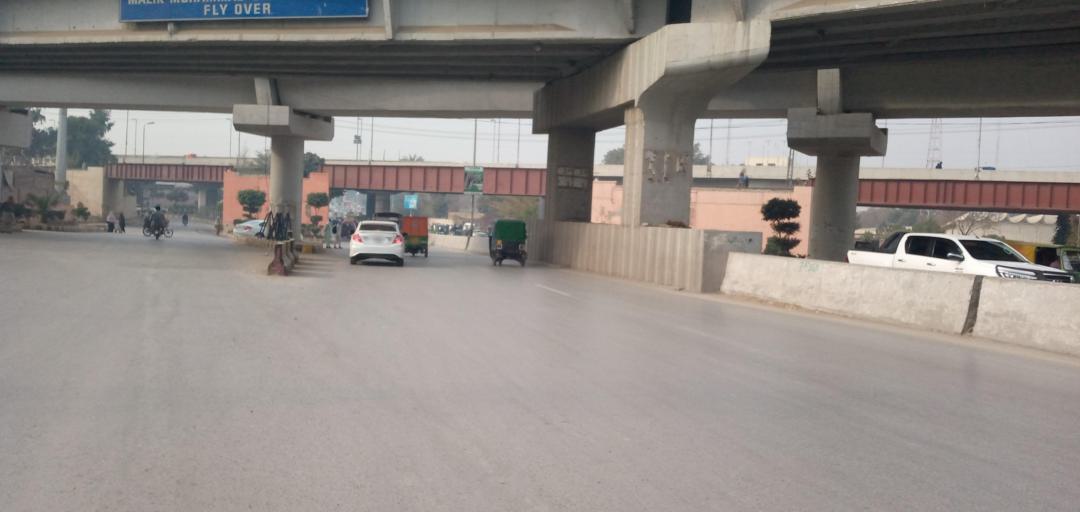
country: PK
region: Khyber Pakhtunkhwa
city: Peshawar
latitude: 34.0144
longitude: 71.5692
